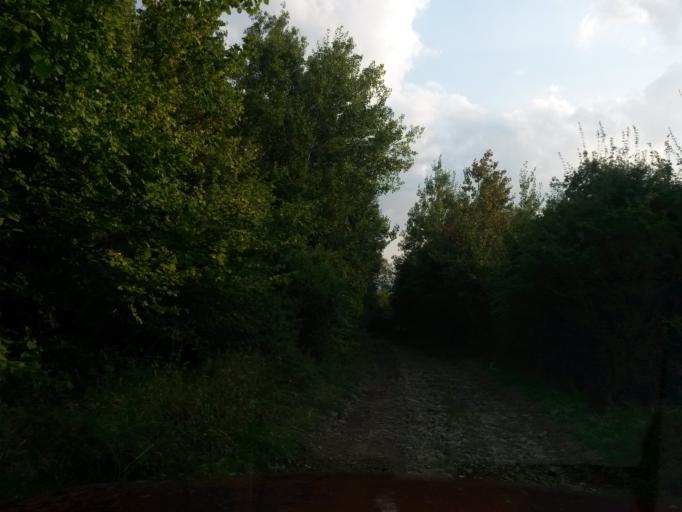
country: SK
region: Kosicky
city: Secovce
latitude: 48.8121
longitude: 21.4796
